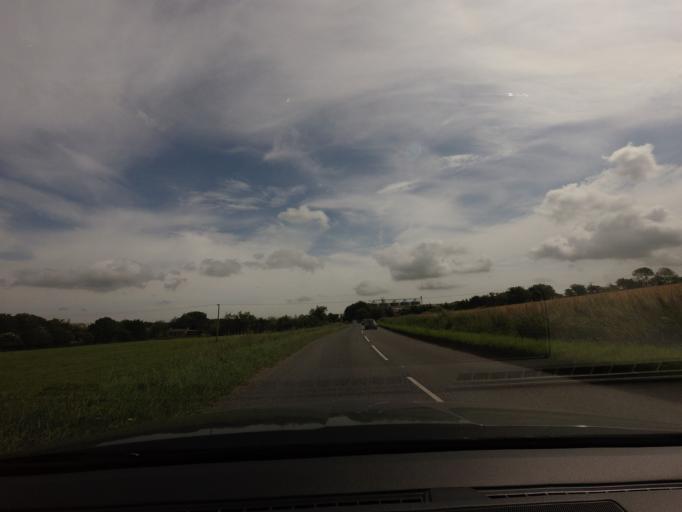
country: GB
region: Scotland
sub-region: Aberdeenshire
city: Mintlaw
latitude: 57.5248
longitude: -1.9854
